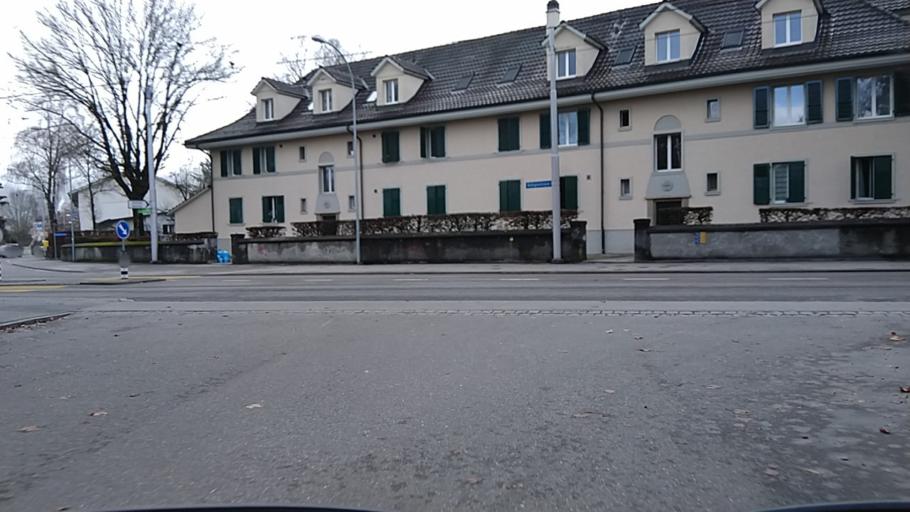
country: CH
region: Bern
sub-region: Bern-Mittelland District
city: Koniz
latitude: 46.9396
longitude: 7.3852
